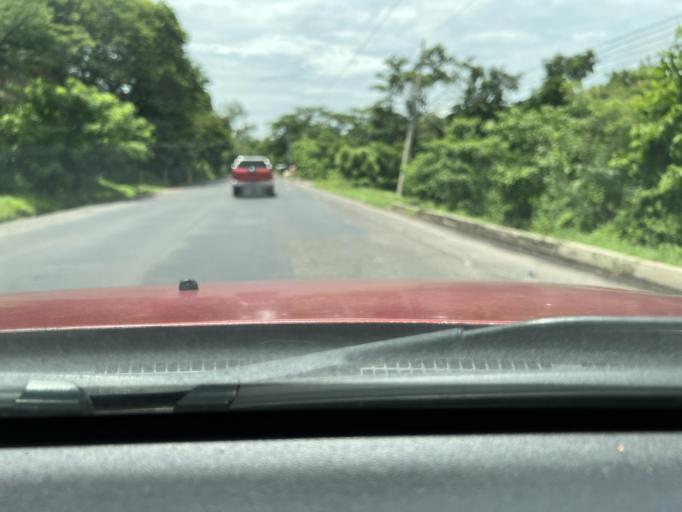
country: SV
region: Usulutan
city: Berlin
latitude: 13.6030
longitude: -88.5848
